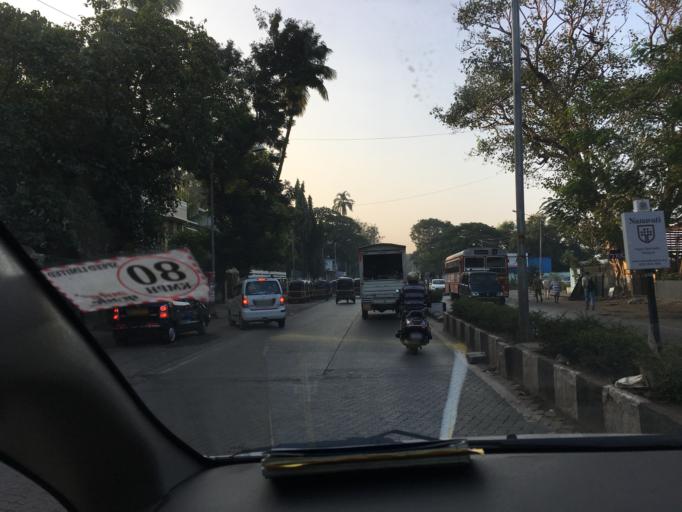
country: IN
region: Maharashtra
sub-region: Mumbai Suburban
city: Mumbai
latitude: 19.1004
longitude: 72.8395
